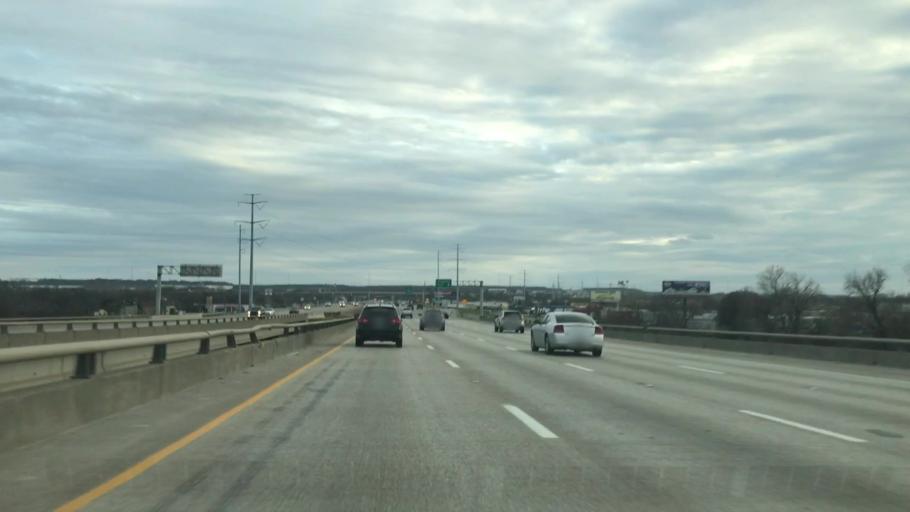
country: US
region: Texas
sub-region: Dallas County
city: Irving
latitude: 32.7829
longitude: -96.9181
